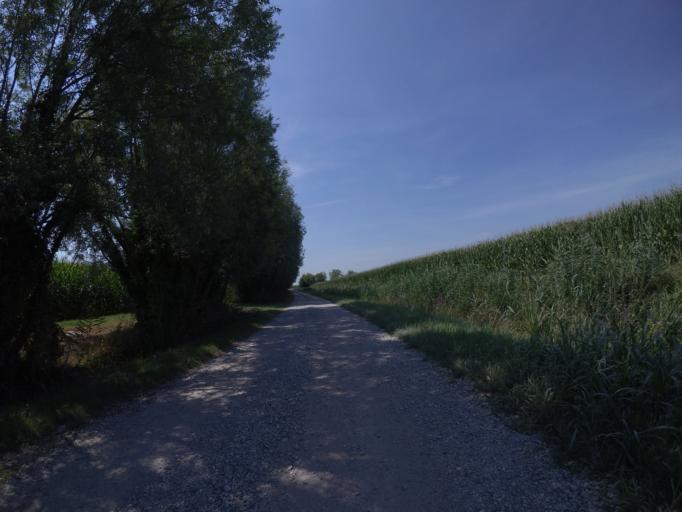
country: IT
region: Friuli Venezia Giulia
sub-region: Provincia di Udine
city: Varmo
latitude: 45.9129
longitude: 12.9889
